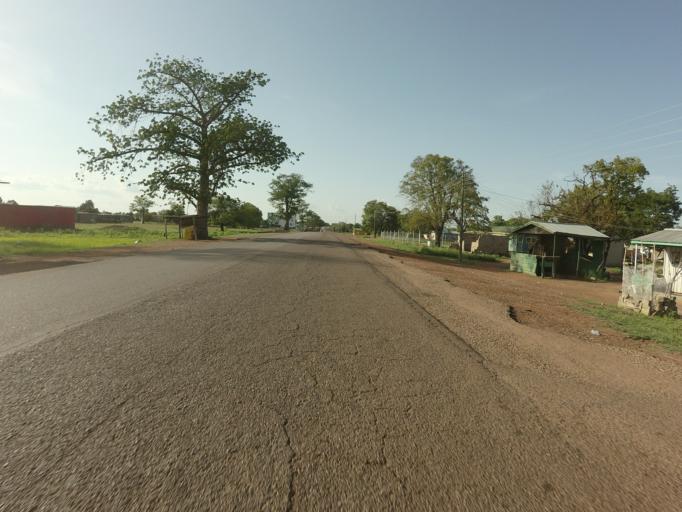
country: GH
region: Upper East
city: Navrongo
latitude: 10.9105
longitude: -1.0902
